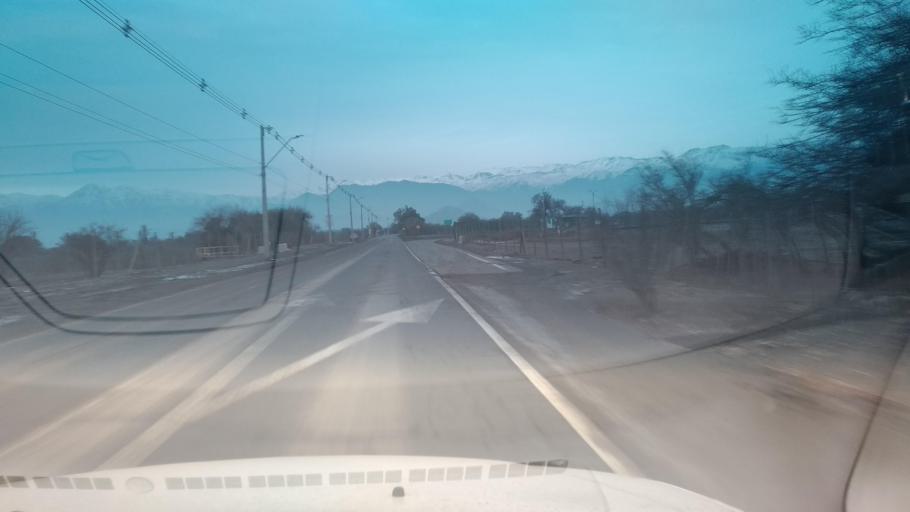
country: CL
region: Santiago Metropolitan
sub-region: Provincia de Chacabuco
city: Chicureo Abajo
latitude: -33.0932
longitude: -70.7429
